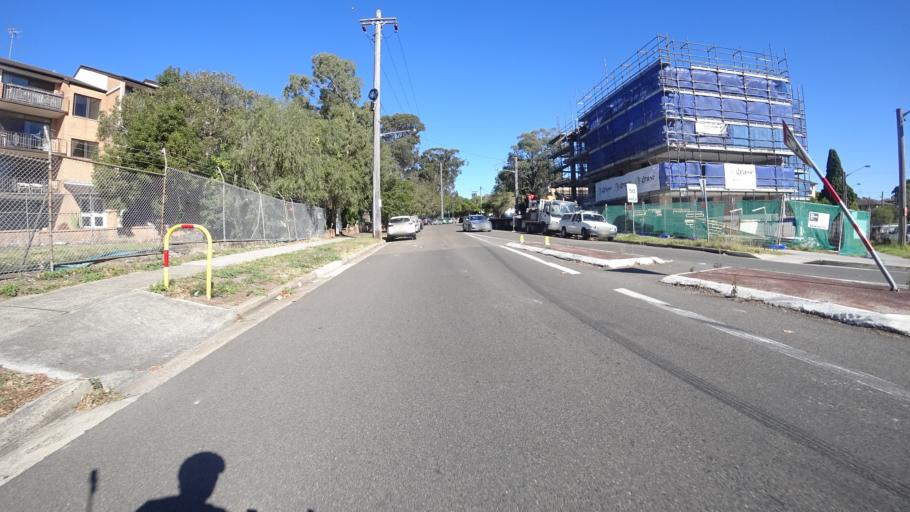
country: AU
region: New South Wales
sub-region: Kogarah
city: Beverly Park
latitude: -33.9673
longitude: 151.1260
